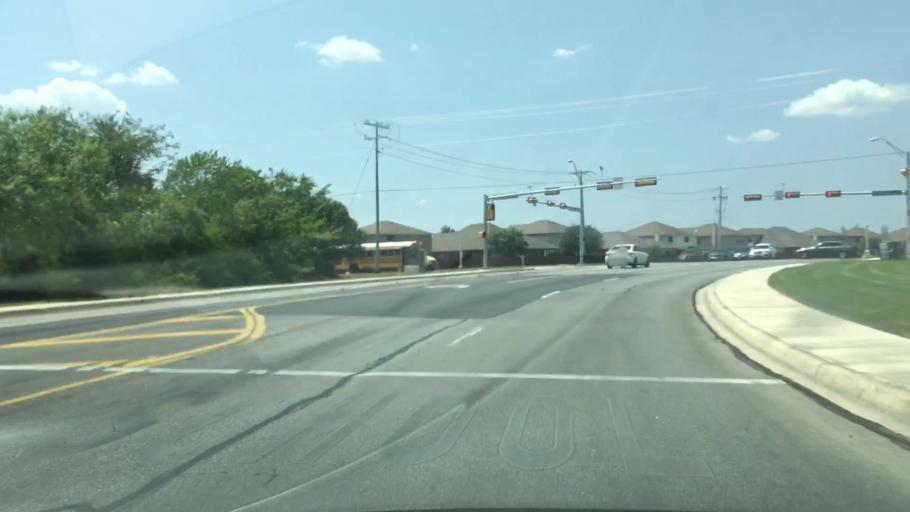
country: US
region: Texas
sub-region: Guadalupe County
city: Cibolo
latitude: 29.5717
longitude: -98.2394
